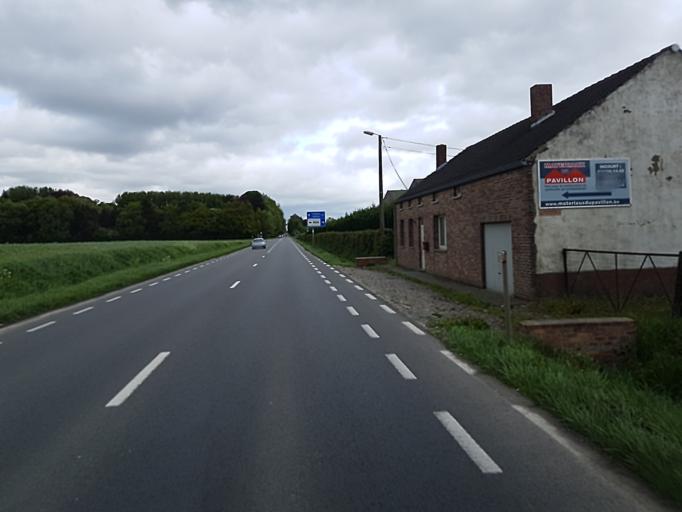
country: BE
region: Wallonia
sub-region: Province du Brabant Wallon
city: Perwez
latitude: 50.6475
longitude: 4.7942
